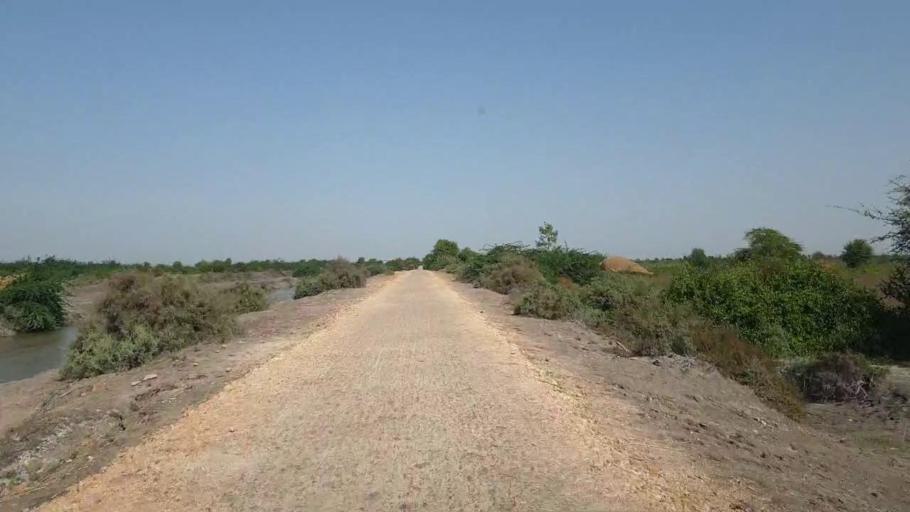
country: PK
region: Sindh
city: Tando Bago
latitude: 24.7231
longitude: 69.0733
